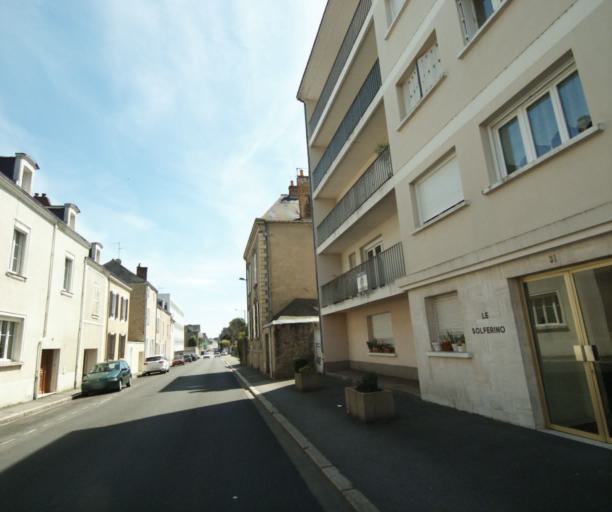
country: FR
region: Pays de la Loire
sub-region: Departement de la Mayenne
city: Laval
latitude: 48.0748
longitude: -0.7653
